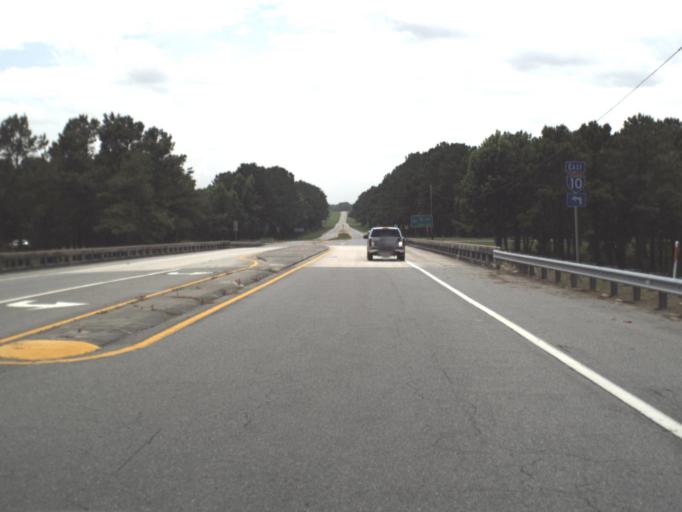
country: US
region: Florida
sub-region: Madison County
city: Madison
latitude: 30.4319
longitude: -83.4556
